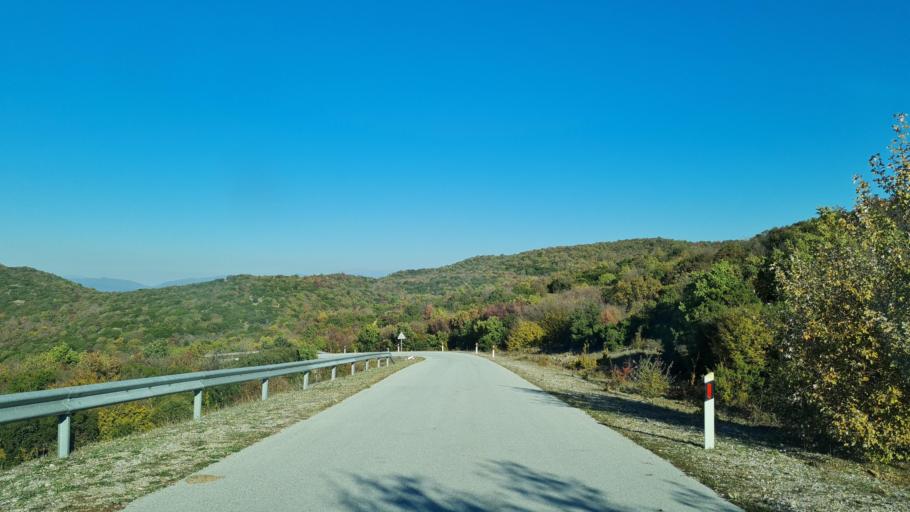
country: MK
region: Bogdanci
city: Bogdanci
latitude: 41.2237
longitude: 22.5529
